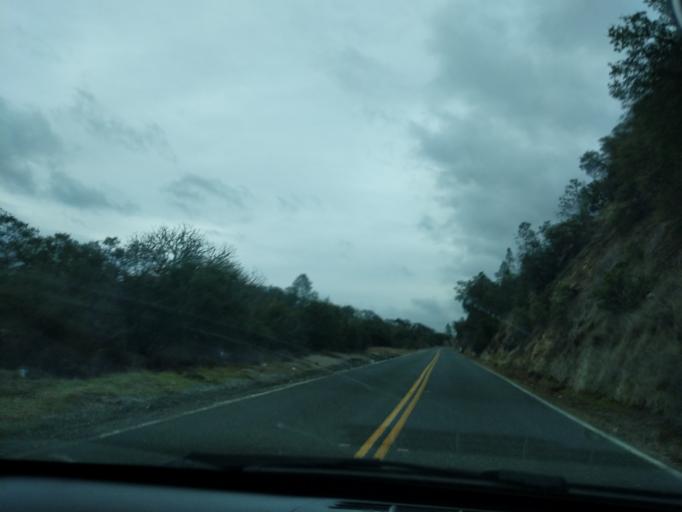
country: US
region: California
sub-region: Monterey County
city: Soledad
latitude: 36.5795
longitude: -121.1903
